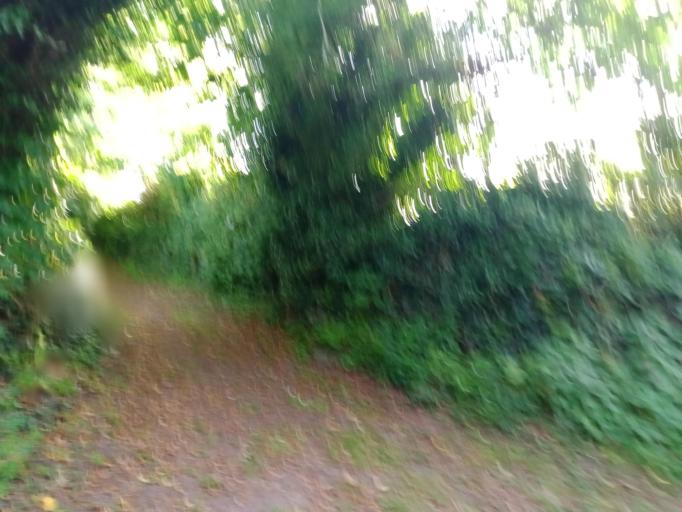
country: IE
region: Leinster
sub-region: Laois
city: Rathdowney
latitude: 52.8152
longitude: -7.4756
